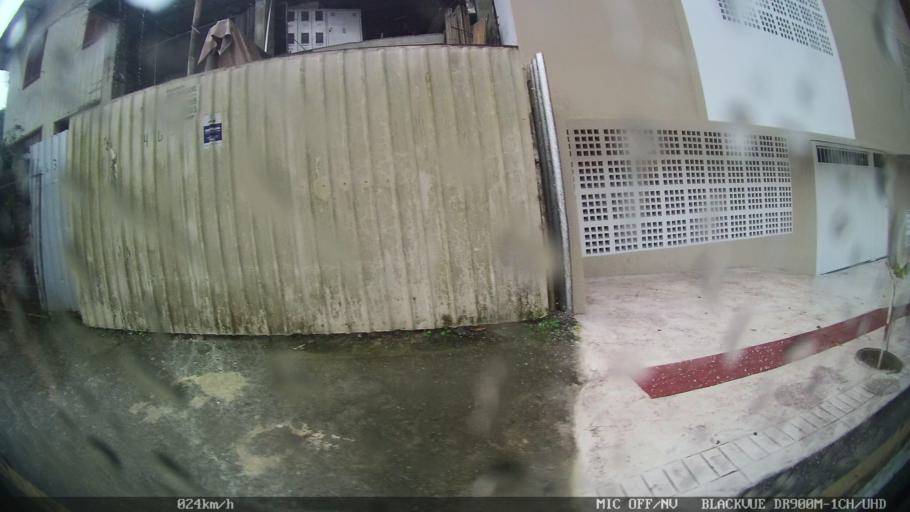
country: BR
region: Santa Catarina
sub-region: Balneario Camboriu
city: Balneario Camboriu
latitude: -26.9734
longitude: -48.6446
